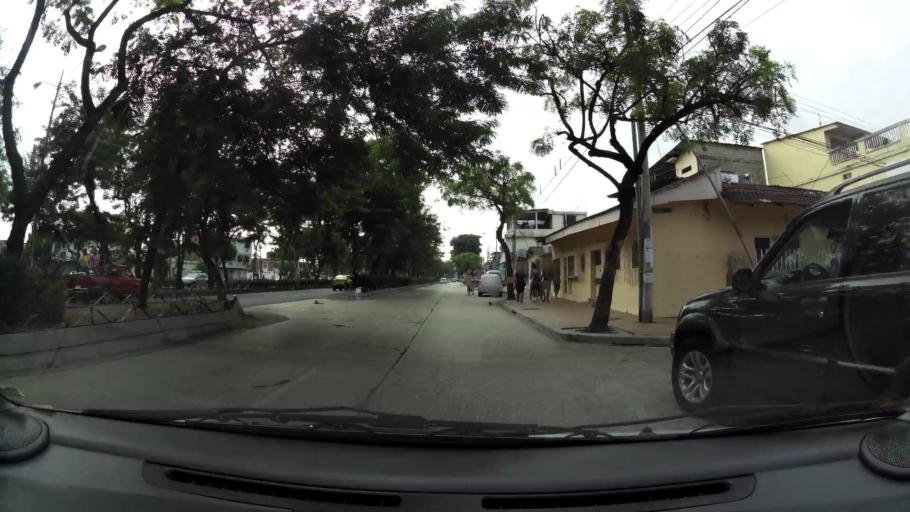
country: EC
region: Guayas
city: Eloy Alfaro
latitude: -2.1398
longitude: -79.8903
